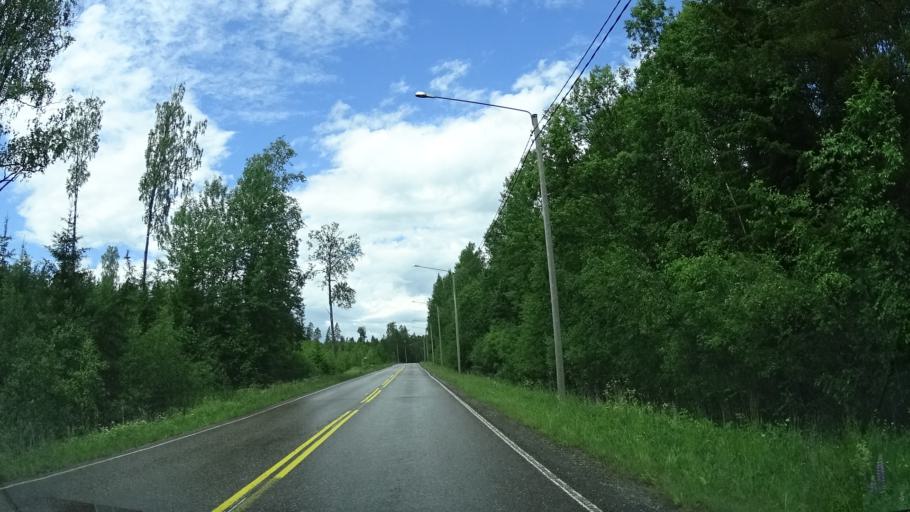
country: FI
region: Uusimaa
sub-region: Helsinki
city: Espoo
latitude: 60.3481
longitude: 24.6516
